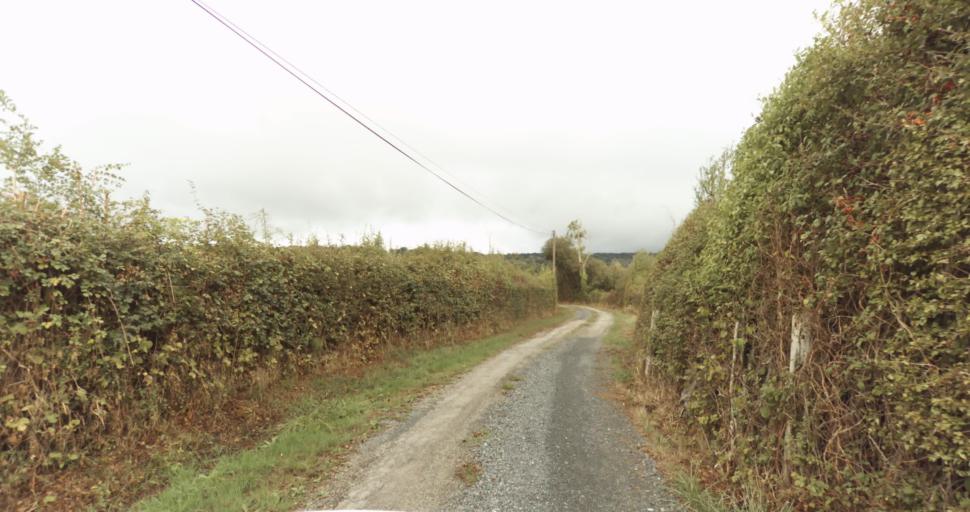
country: FR
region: Lower Normandy
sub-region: Departement du Calvados
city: Livarot
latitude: 48.9314
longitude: 0.1069
